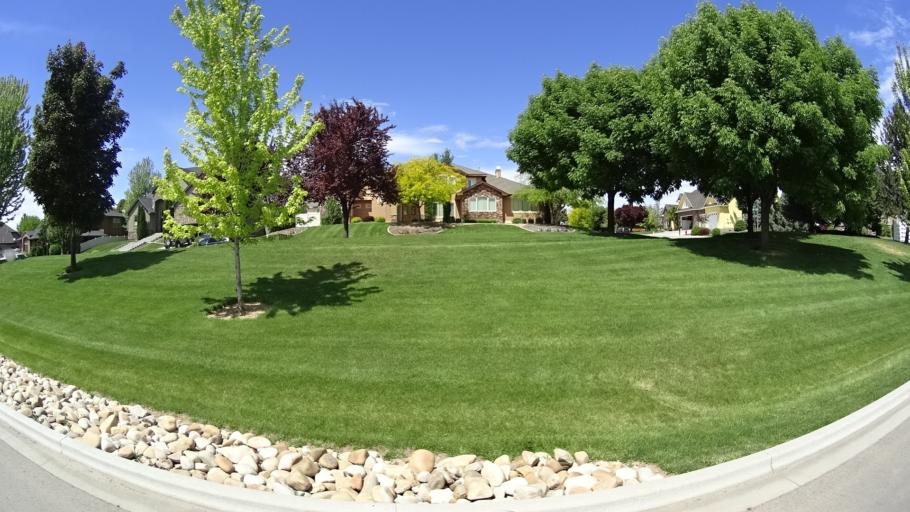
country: US
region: Idaho
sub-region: Ada County
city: Meridian
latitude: 43.5757
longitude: -116.3855
